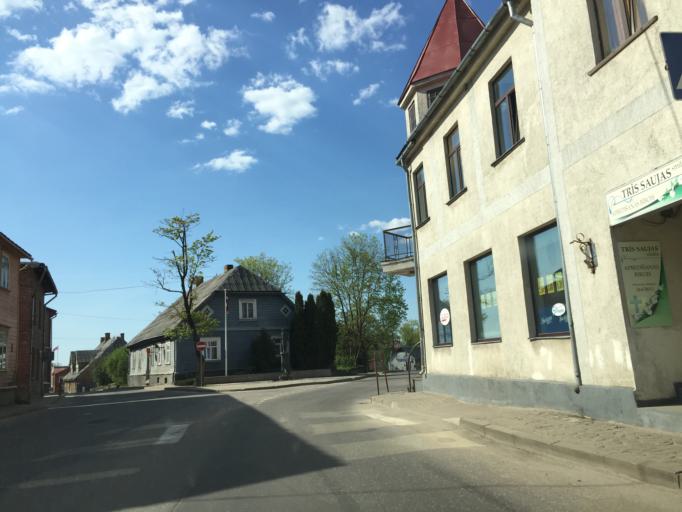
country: LV
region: Limbazu Rajons
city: Limbazi
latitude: 57.5140
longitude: 24.7162
